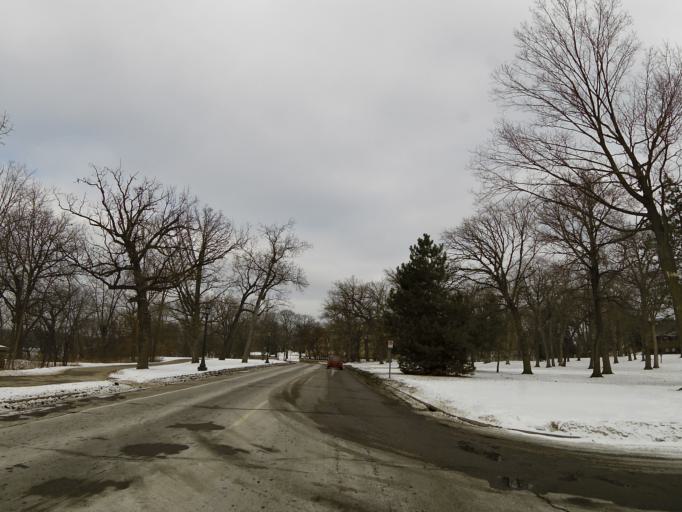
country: US
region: Minnesota
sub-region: Ramsey County
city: Lauderdale
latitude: 44.9379
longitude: -93.1978
